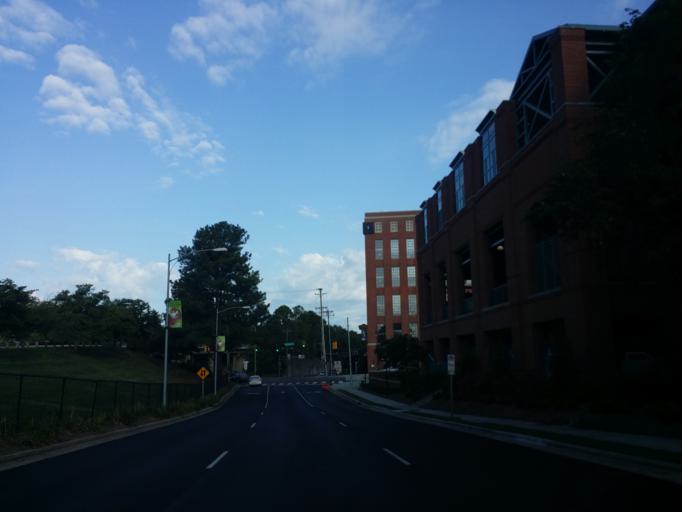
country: US
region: North Carolina
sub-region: Durham County
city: Durham
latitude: 35.9910
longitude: -78.9045
